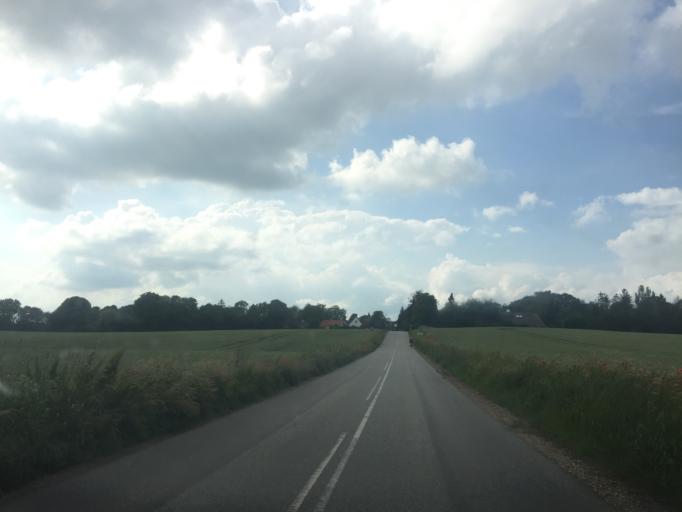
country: DK
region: Capital Region
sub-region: Hoje-Taastrup Kommune
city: Flong
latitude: 55.6904
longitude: 12.1704
